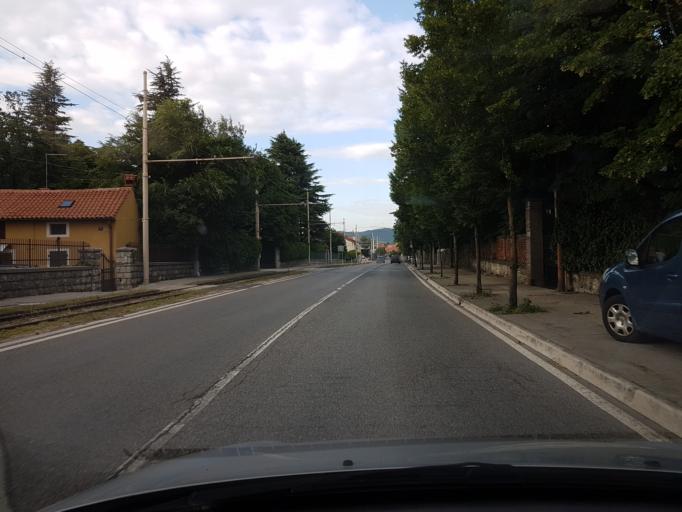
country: IT
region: Friuli Venezia Giulia
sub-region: Provincia di Trieste
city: Villa Opicina
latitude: 45.6849
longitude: 13.7851
